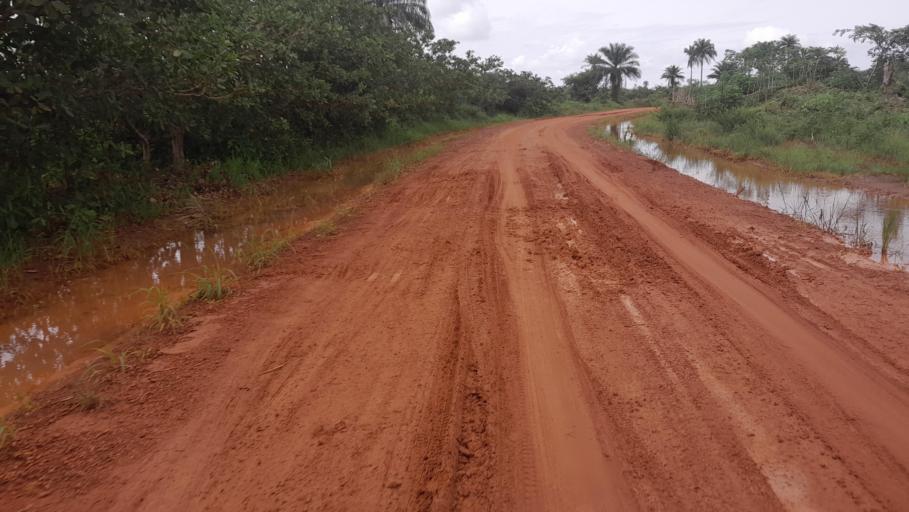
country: GN
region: Boke
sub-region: Boffa
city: Boffa
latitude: 10.0622
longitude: -13.8678
